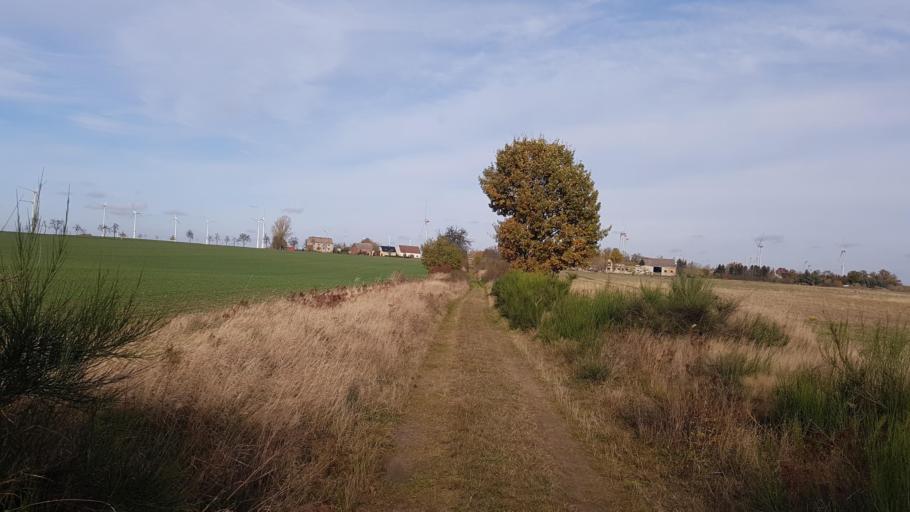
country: DE
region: Saxony-Anhalt
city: Zahna
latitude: 51.9715
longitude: 12.8287
